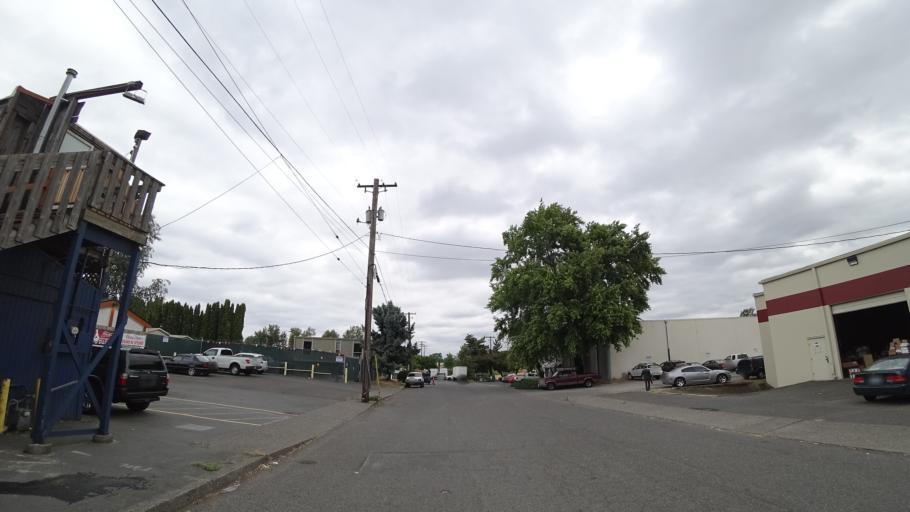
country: US
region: Washington
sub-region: Clark County
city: Vancouver
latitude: 45.5838
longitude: -122.6725
